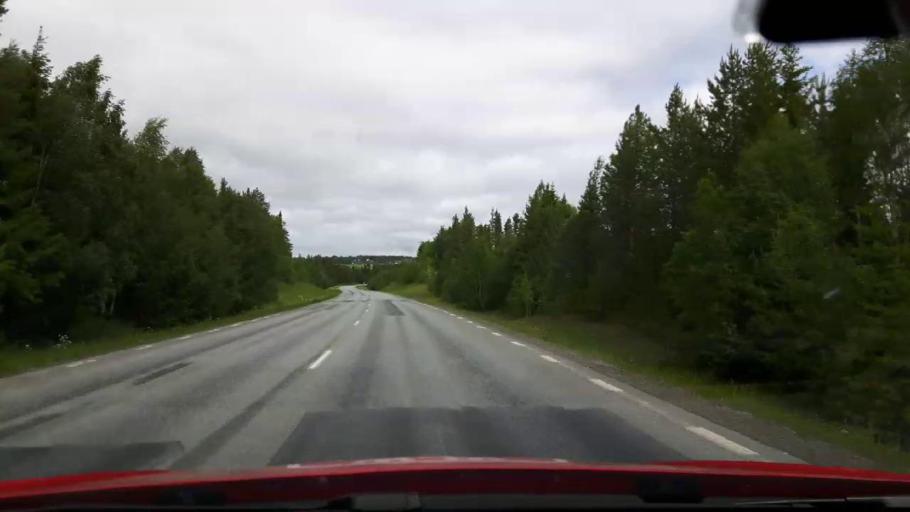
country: SE
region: Jaemtland
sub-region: Krokoms Kommun
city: Krokom
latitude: 63.3447
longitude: 14.4731
